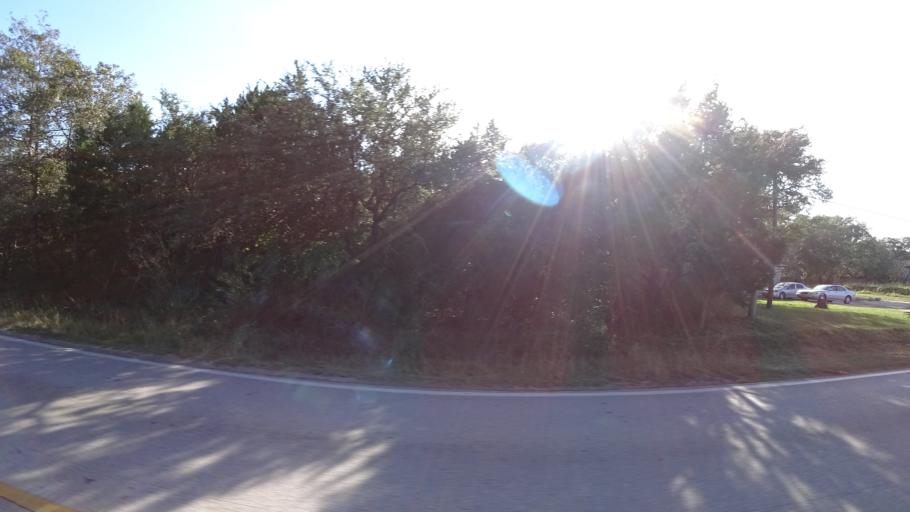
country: US
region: Texas
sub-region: Travis County
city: Bee Cave
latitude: 30.2458
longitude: -97.9263
